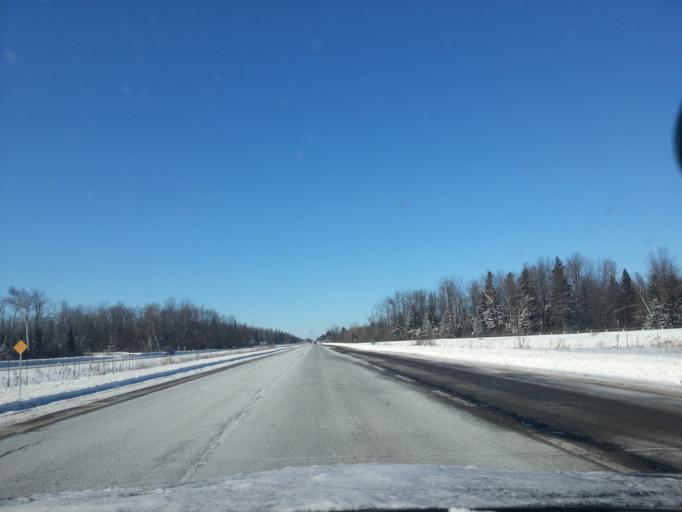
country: CA
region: Ontario
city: Carleton Place
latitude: 45.3132
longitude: -76.0570
